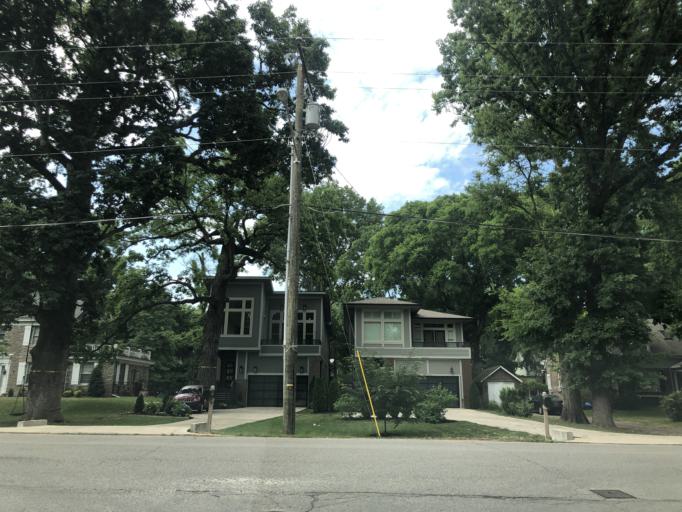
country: US
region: Tennessee
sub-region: Davidson County
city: Oak Hill
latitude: 36.1172
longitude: -86.7835
